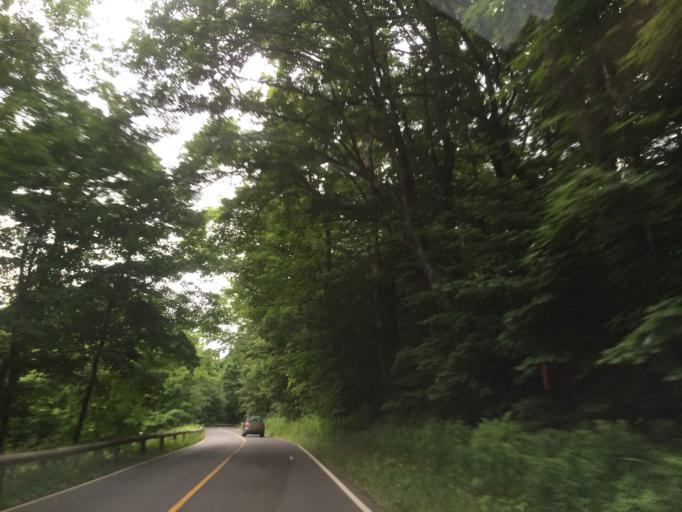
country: US
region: Massachusetts
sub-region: Berkshire County
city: Adams
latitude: 42.6168
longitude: -73.1999
